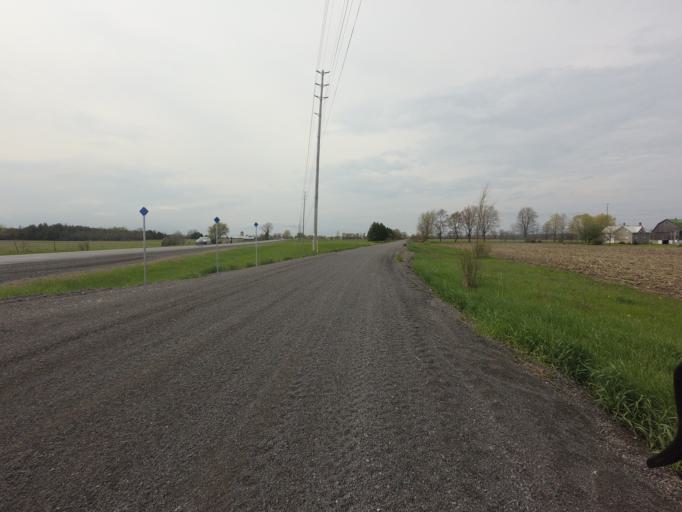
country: CA
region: Ontario
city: Carleton Place
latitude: 45.1840
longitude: -76.1584
